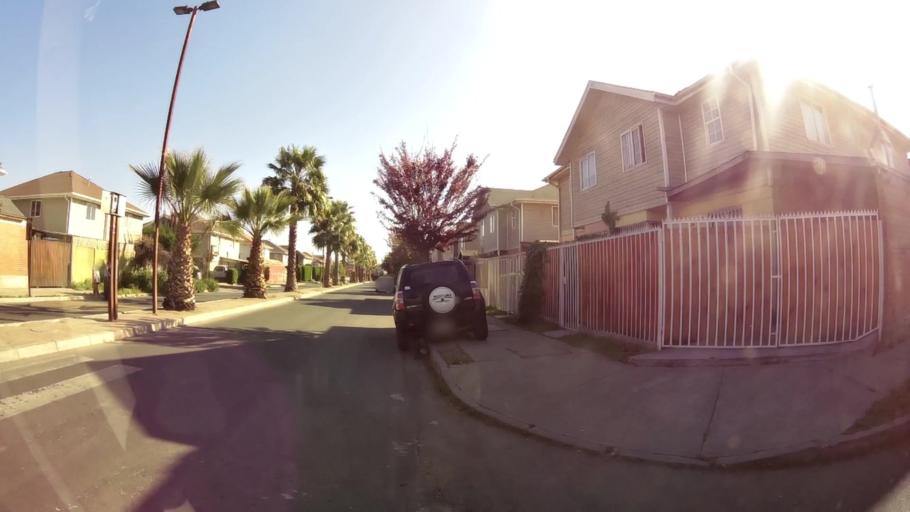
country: CL
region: Santiago Metropolitan
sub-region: Provincia de Santiago
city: Lo Prado
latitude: -33.4899
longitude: -70.7821
